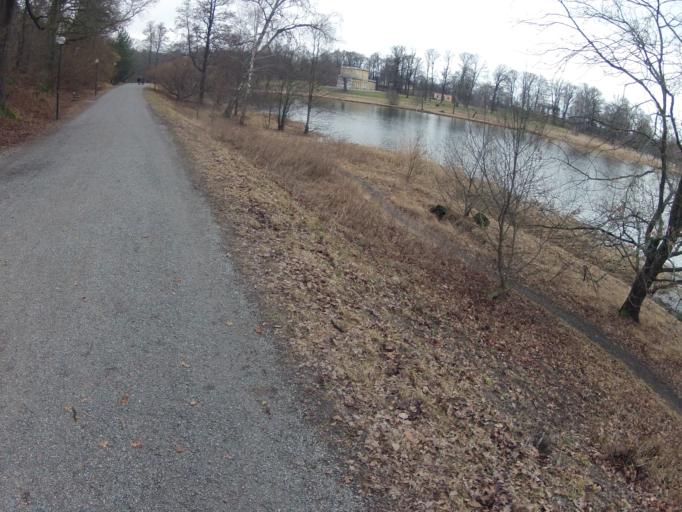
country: SE
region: Stockholm
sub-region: Norrtalje Kommun
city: Bergshamra
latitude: 59.3603
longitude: 18.0396
